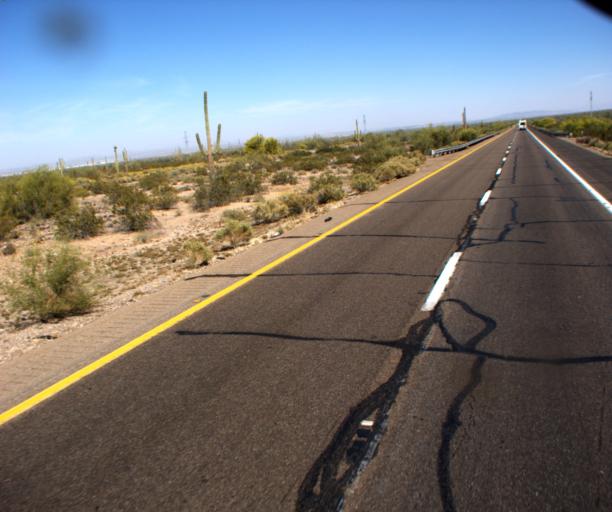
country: US
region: Arizona
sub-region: Pinal County
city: Maricopa
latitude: 32.8334
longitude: -112.1100
